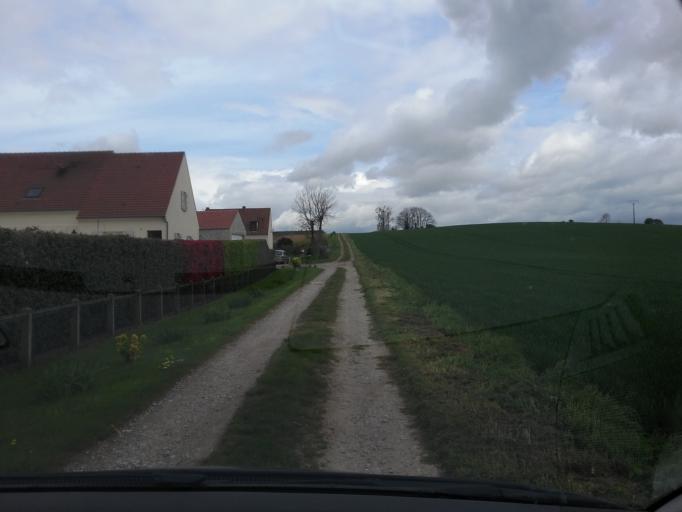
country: FR
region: Picardie
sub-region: Departement de l'Oise
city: Grandfresnoy
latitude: 49.3663
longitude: 2.6631
